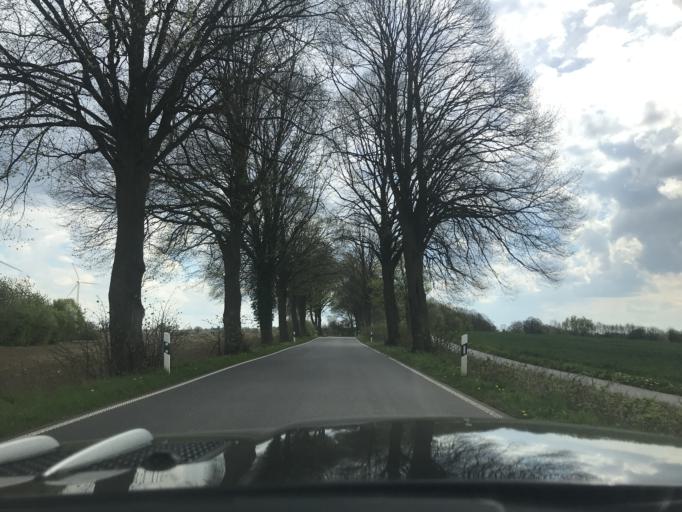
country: DE
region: Schleswig-Holstein
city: Timmendorfer Strand
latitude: 53.9455
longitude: 10.7893
